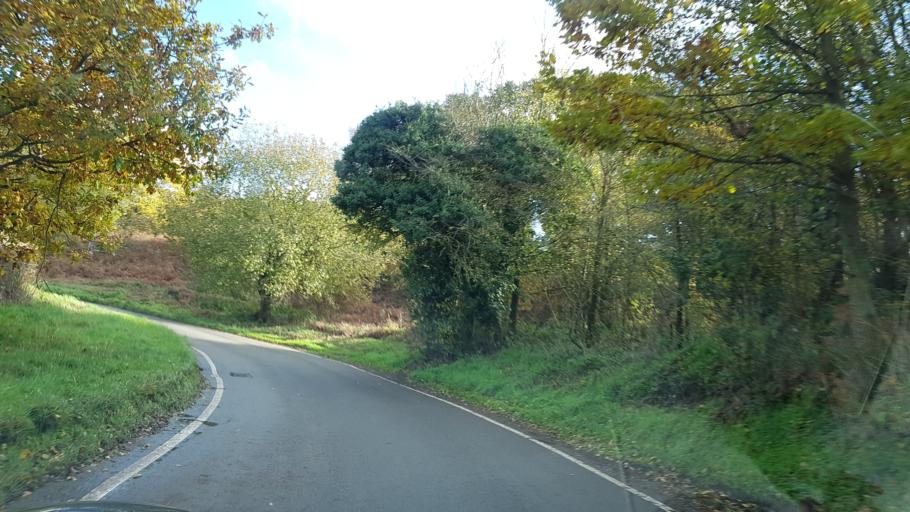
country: GB
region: England
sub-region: Surrey
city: Seale
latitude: 51.2212
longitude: -0.6869
